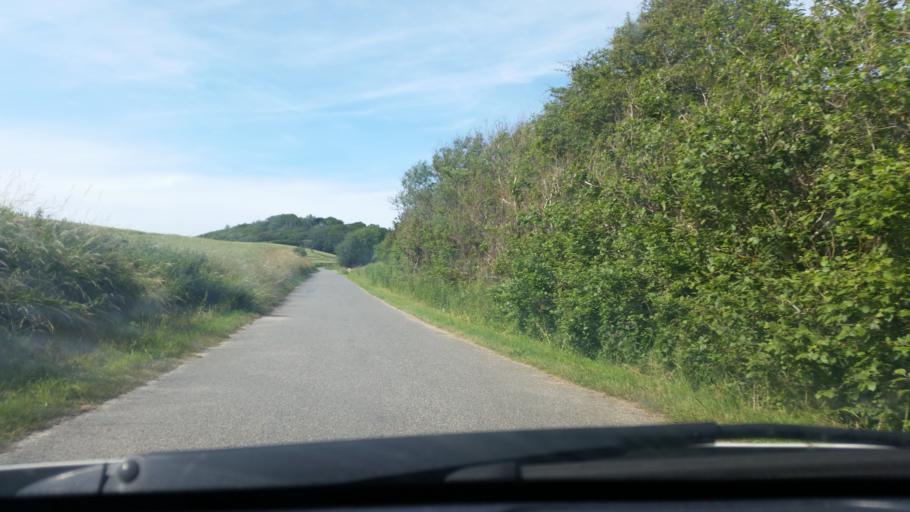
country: DK
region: Central Jutland
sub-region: Samso Kommune
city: Tranebjerg
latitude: 55.7713
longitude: 10.5526
